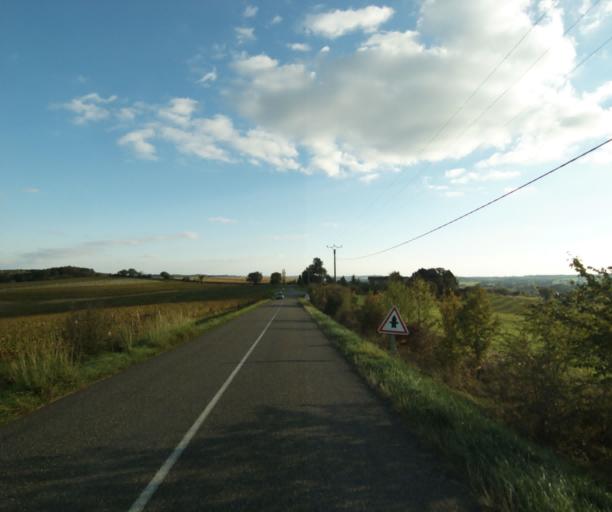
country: FR
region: Midi-Pyrenees
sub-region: Departement du Gers
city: Eauze
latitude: 43.7457
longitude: 0.1358
